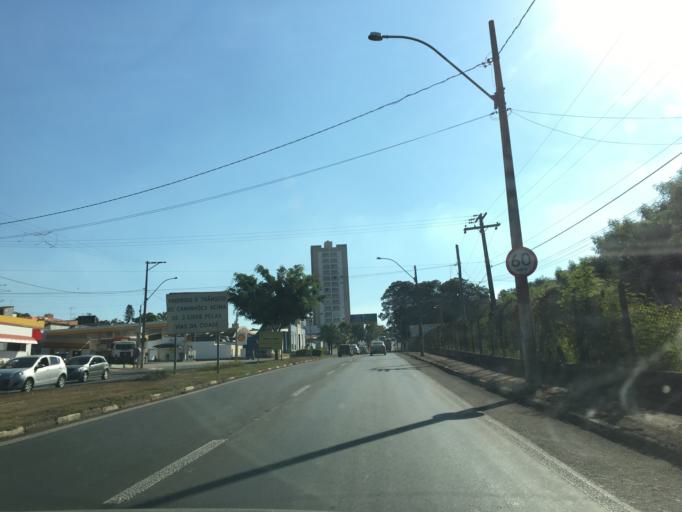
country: BR
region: Sao Paulo
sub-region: Piracicaba
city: Piracicaba
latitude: -22.7160
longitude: -47.6272
